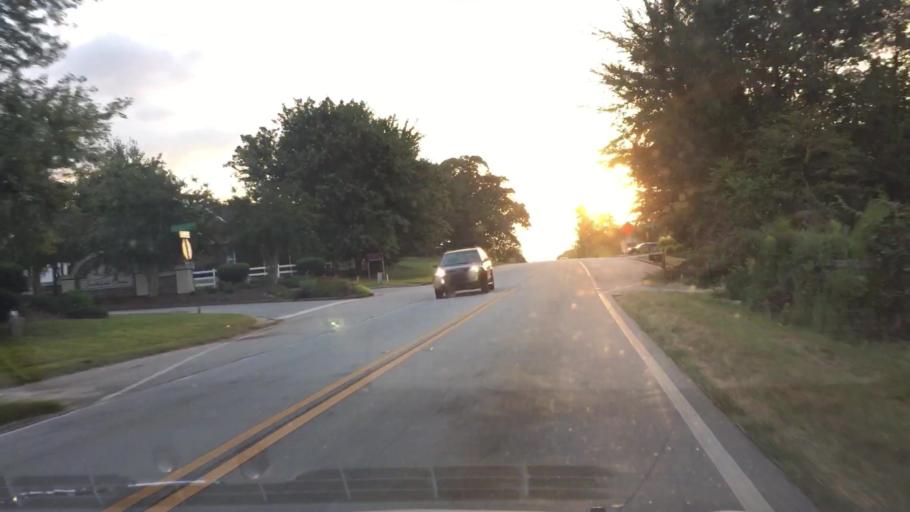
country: US
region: Georgia
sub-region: Henry County
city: McDonough
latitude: 33.5075
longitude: -84.1251
